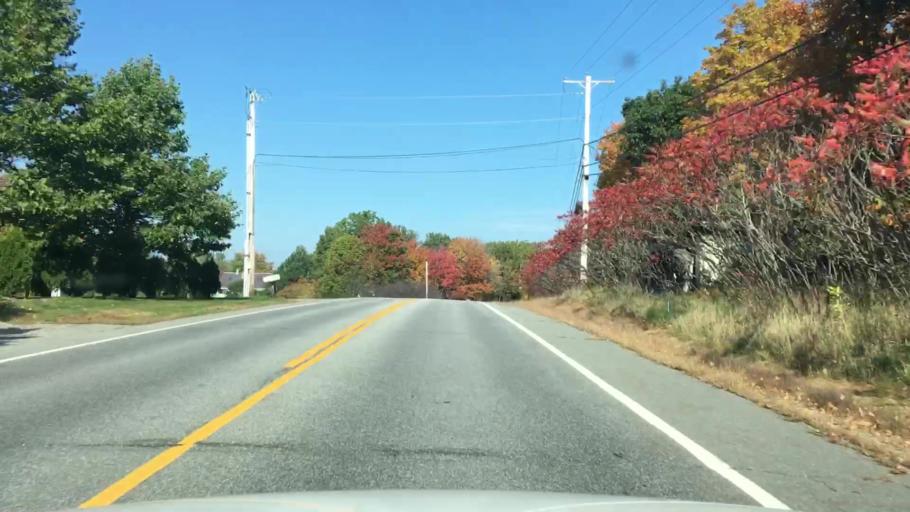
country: US
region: Maine
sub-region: Sagadahoc County
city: Topsham
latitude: 43.9774
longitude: -69.9603
